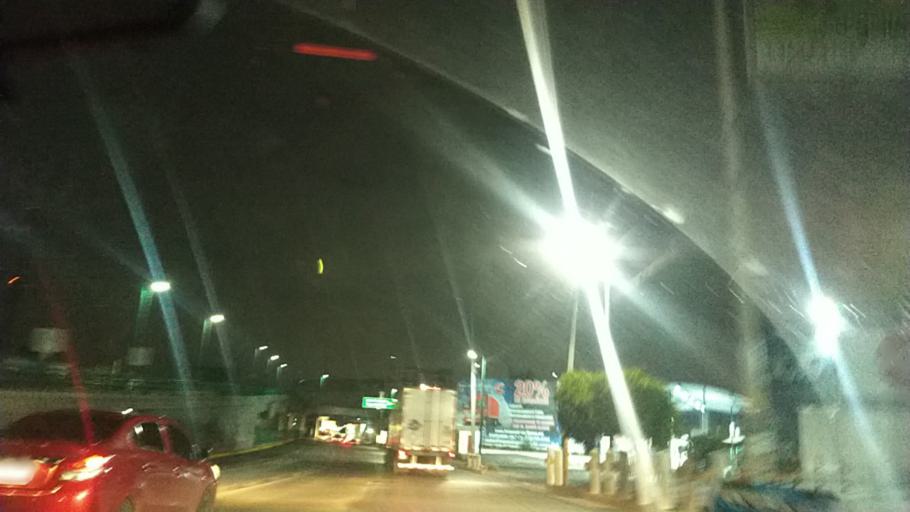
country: MX
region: Mexico
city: Coacalco
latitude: 19.6362
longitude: -99.1100
